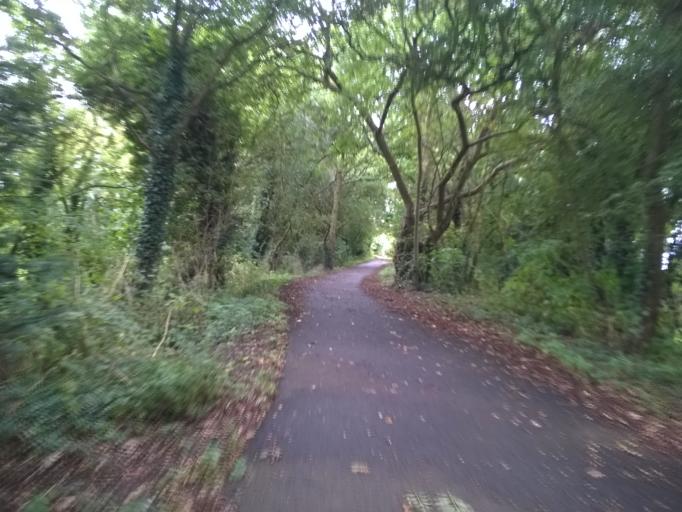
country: GB
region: England
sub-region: Leicestershire
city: Glenfield
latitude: 52.6521
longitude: -1.2061
